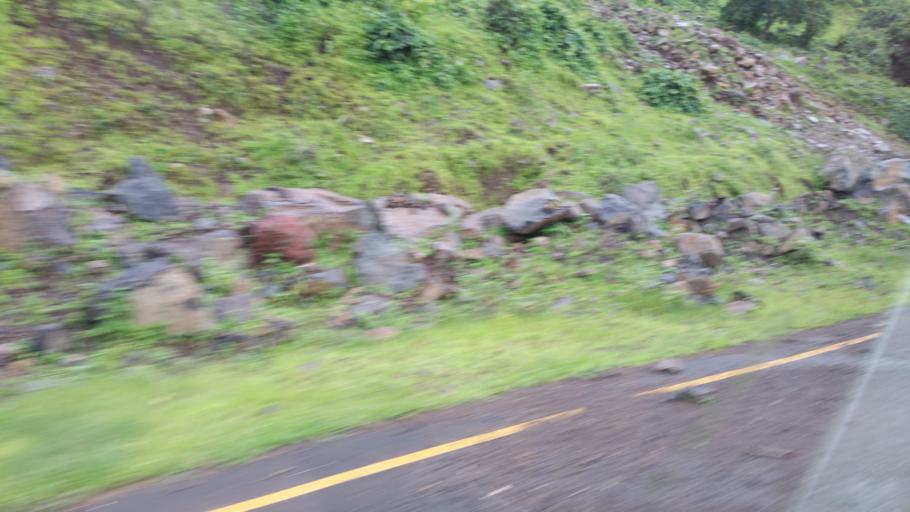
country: ET
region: Amhara
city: Debark'
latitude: 13.3672
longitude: 37.9432
